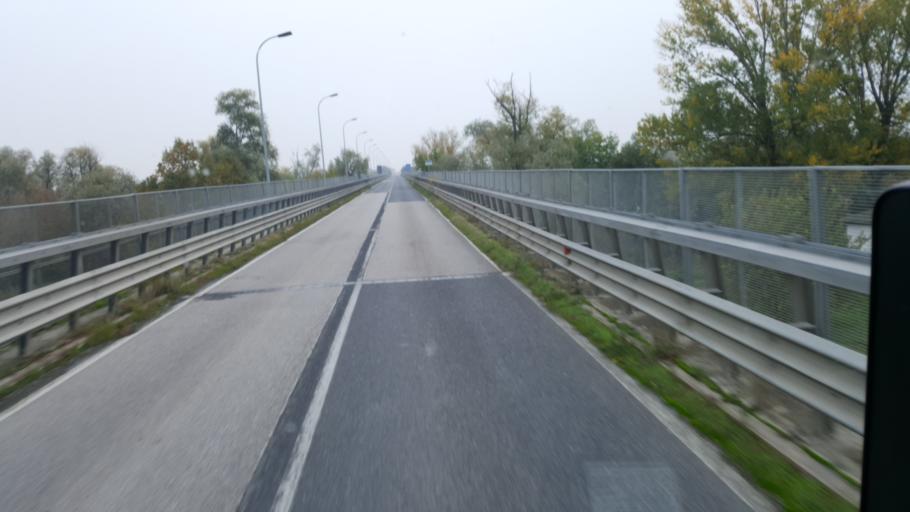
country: IT
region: Veneto
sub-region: Provincia di Rovigo
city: Ficarolo
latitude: 44.9455
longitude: 11.4224
